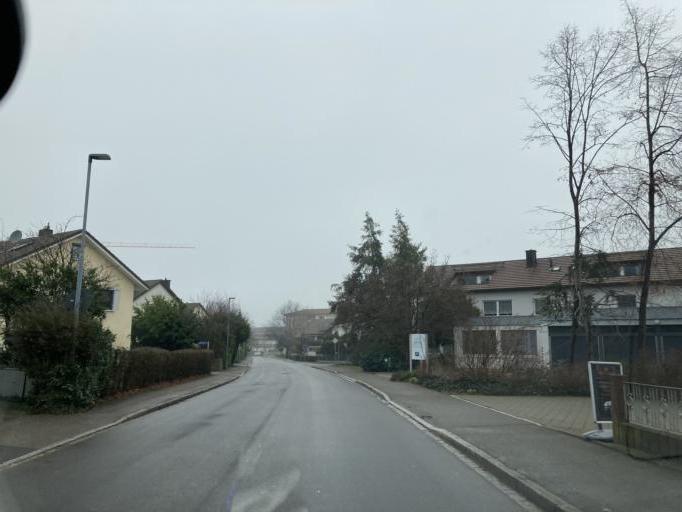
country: DE
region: Baden-Wuerttemberg
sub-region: Freiburg Region
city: Mullheim
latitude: 47.8115
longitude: 7.6220
